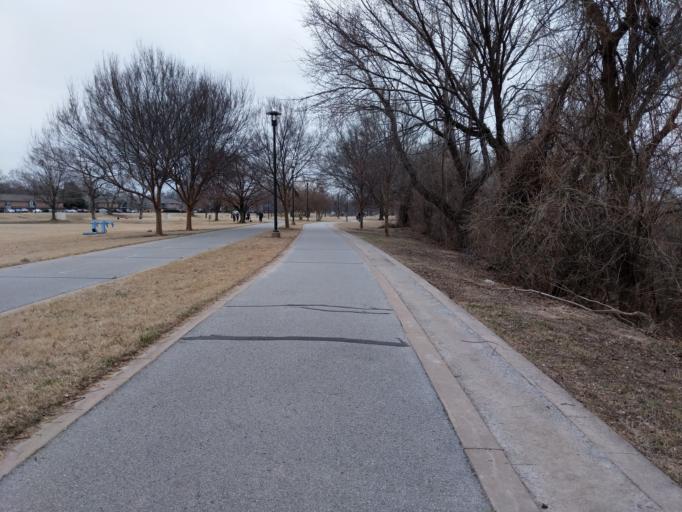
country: US
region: Oklahoma
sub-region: Tulsa County
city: Tulsa
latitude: 36.1090
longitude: -95.9843
